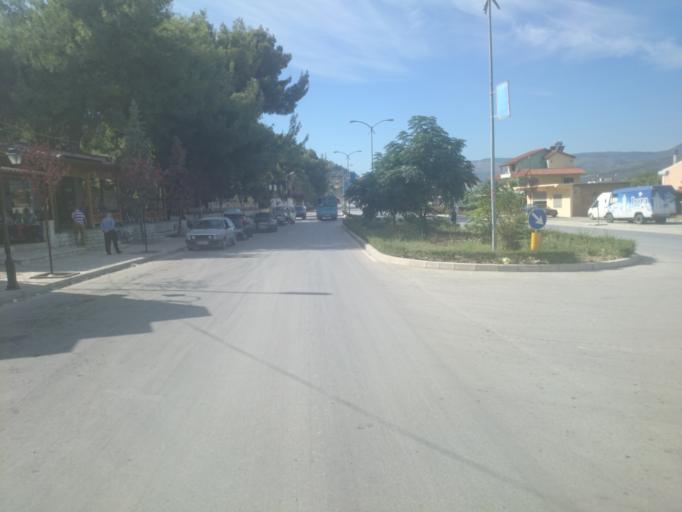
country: AL
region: Berat
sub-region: Rrethi i Beratit
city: Otllak
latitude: 40.7248
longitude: 19.9433
